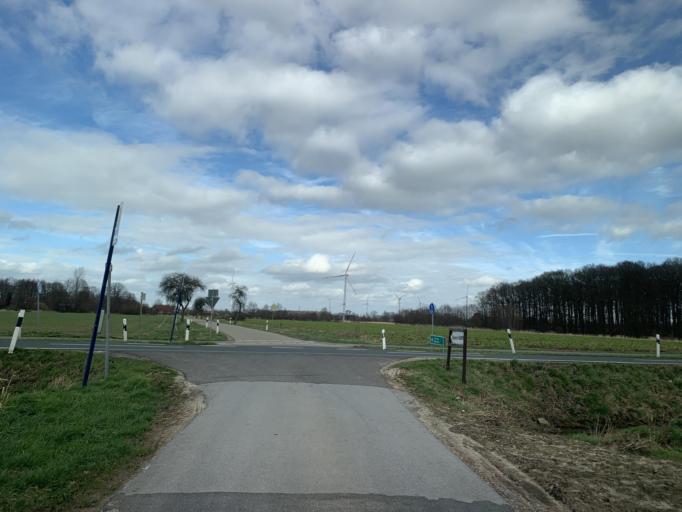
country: DE
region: North Rhine-Westphalia
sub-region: Regierungsbezirk Munster
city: Havixbeck
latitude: 52.0147
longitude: 7.4245
